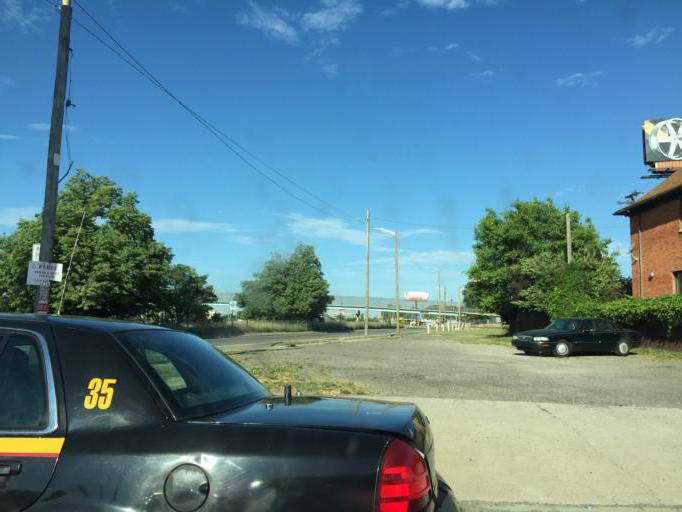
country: US
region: Michigan
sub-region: Wayne County
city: Detroit
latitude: 42.3351
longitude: -83.0690
